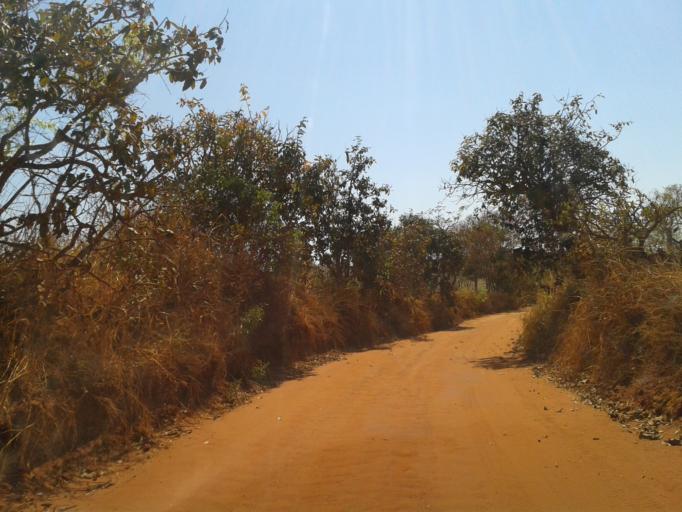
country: BR
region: Minas Gerais
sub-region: Ituiutaba
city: Ituiutaba
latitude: -19.0624
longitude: -49.3542
